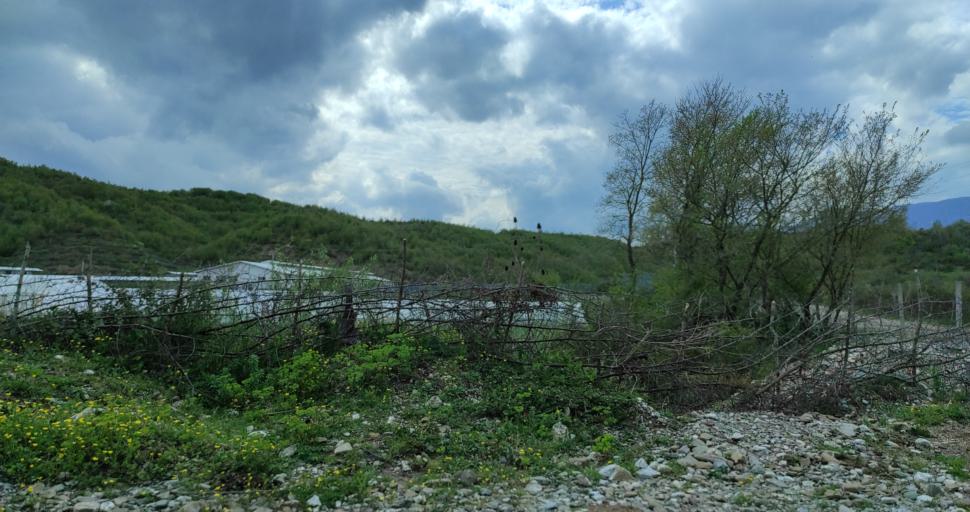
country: AL
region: Shkoder
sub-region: Rrethi i Shkodres
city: Dajc
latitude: 42.0363
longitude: 19.4021
